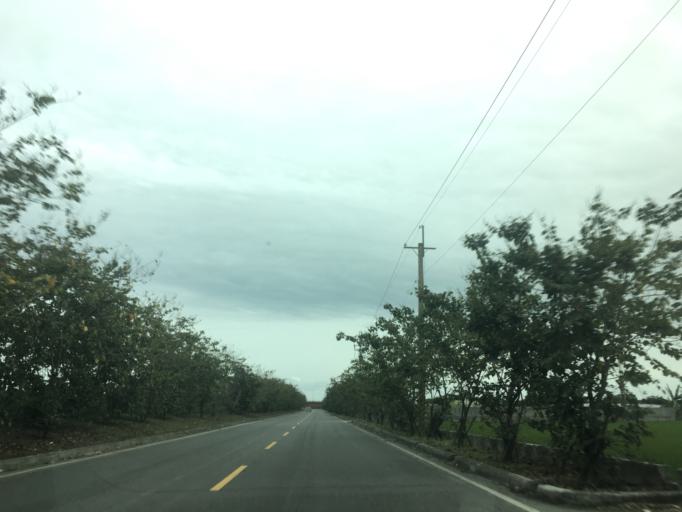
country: TW
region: Taiwan
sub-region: Taitung
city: Taitung
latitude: 22.7952
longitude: 121.1376
